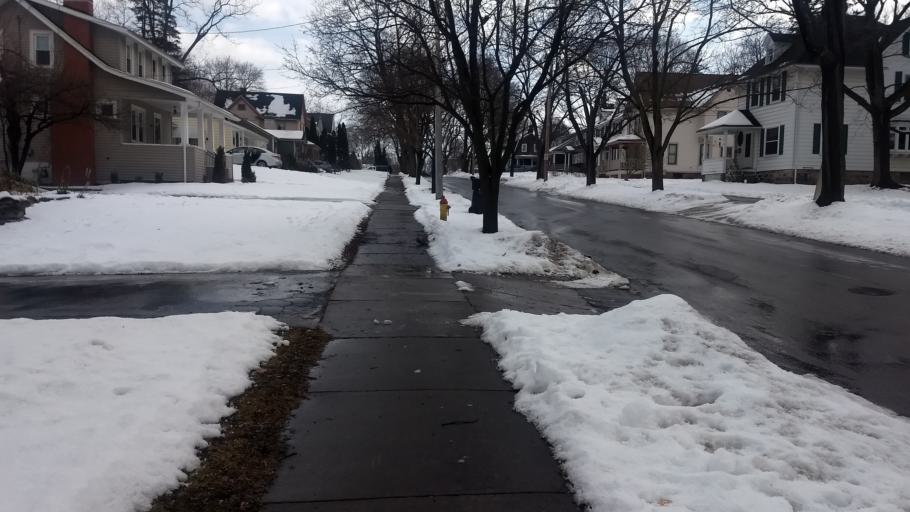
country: US
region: New York
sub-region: Livingston County
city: Geneseo
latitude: 42.7975
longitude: -77.8095
